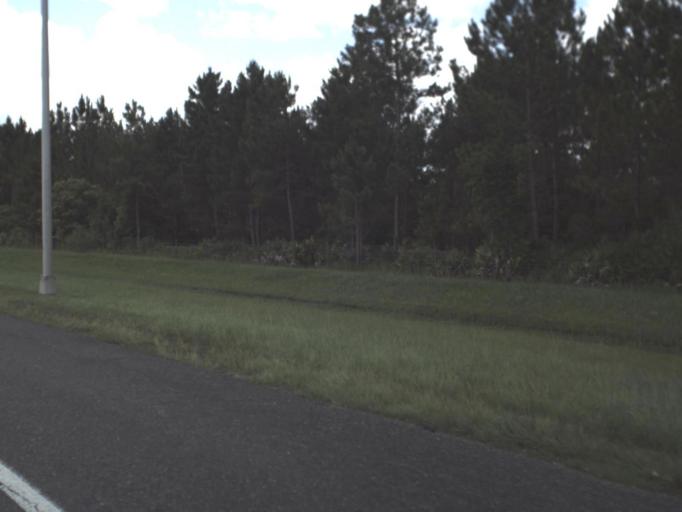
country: US
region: Florida
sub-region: Saint Johns County
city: Saint Augustine Shores
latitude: 29.7524
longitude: -81.3485
